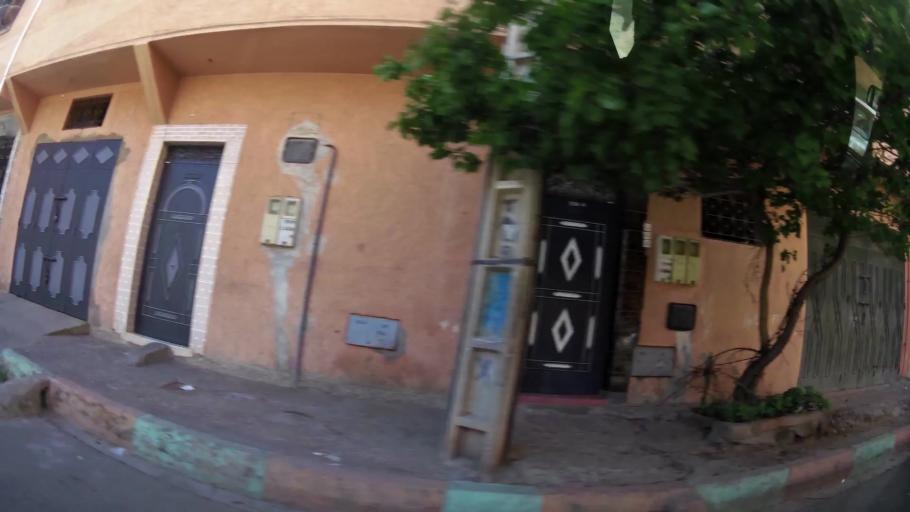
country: MA
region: Marrakech-Tensift-Al Haouz
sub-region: Marrakech
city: Marrakesh
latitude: 31.6430
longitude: -8.0663
